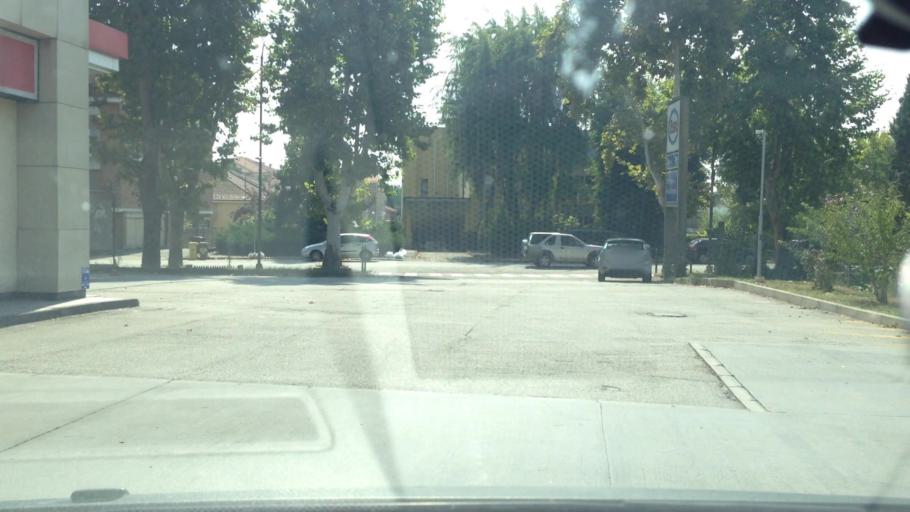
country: IT
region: Piedmont
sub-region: Provincia di Asti
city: Asti
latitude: 44.9054
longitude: 8.2269
